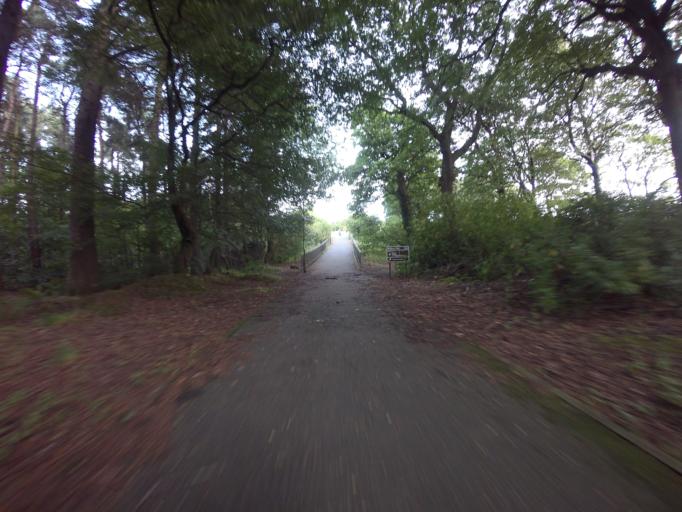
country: GB
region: Scotland
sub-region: West Lothian
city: Livingston
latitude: 55.9124
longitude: -3.5616
